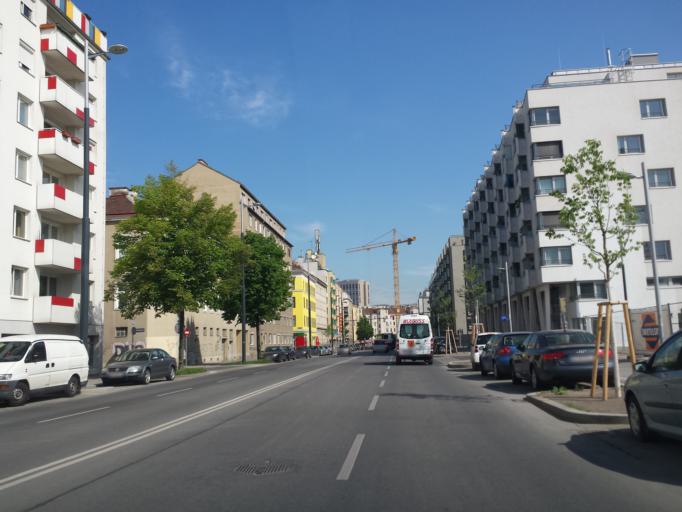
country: AT
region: Vienna
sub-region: Wien Stadt
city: Vienna
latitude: 48.1788
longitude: 16.3799
